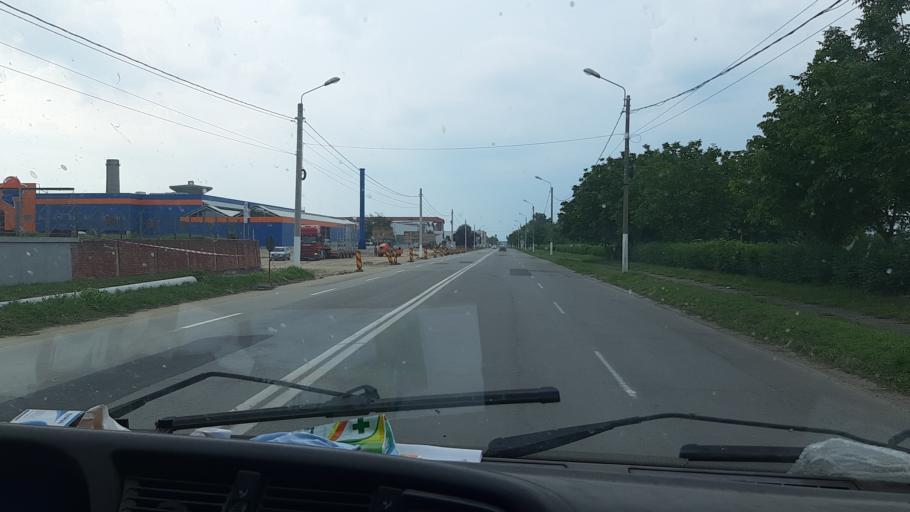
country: RO
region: Timis
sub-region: Municipiul Lugoj
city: Lugoj
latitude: 45.7028
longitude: 21.8921
